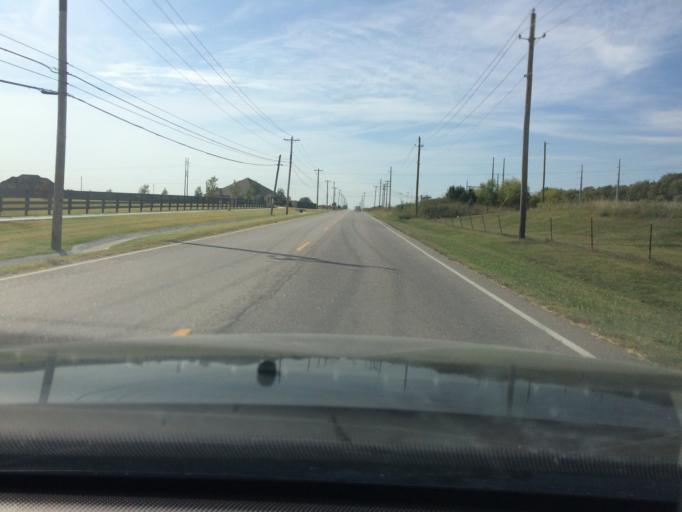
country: US
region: Oklahoma
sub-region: Tulsa County
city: Broken Arrow
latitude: 36.1045
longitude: -95.7851
